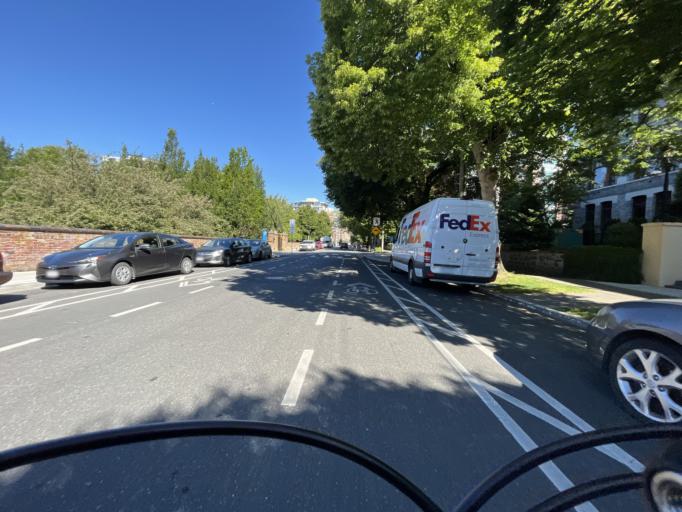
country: CA
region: British Columbia
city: Victoria
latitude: 48.4195
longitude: -123.3623
